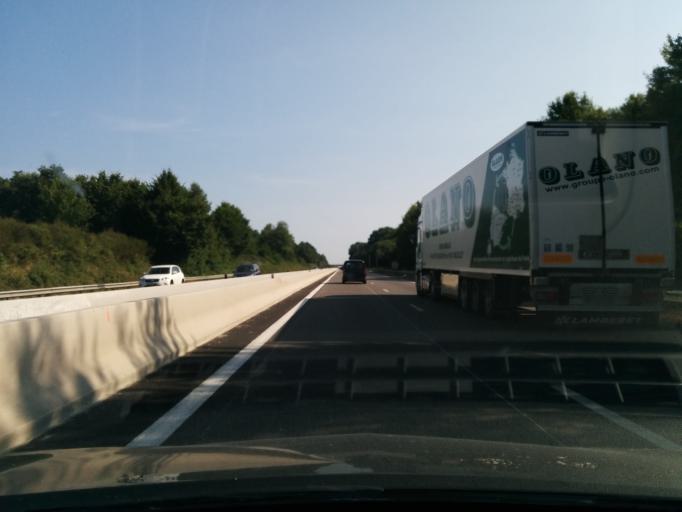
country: FR
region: Limousin
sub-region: Departement de la Haute-Vienne
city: Le Palais-sur-Vienne
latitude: 45.8723
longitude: 1.2878
